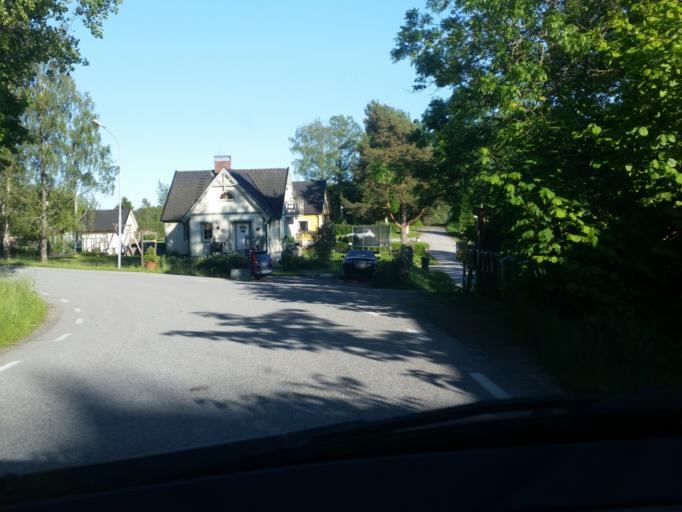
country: SE
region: Vaestra Goetaland
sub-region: Fargelanda Kommun
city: Faergelanda
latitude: 58.5159
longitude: 11.9800
